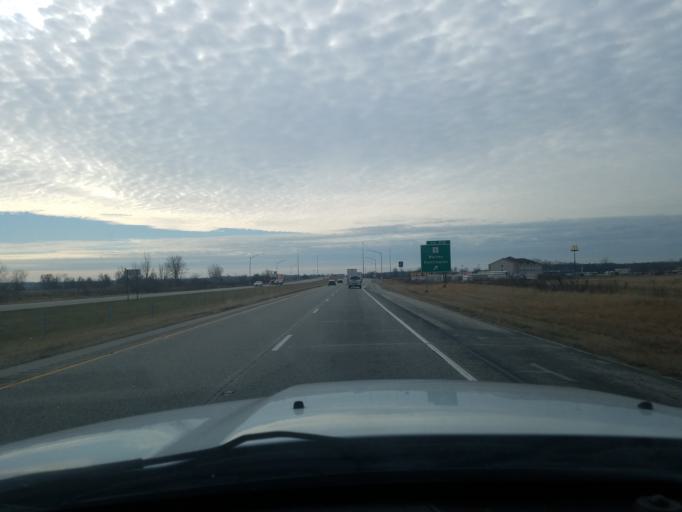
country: US
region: Indiana
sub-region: Huntington County
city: Warren
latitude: 40.7247
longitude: -85.4311
